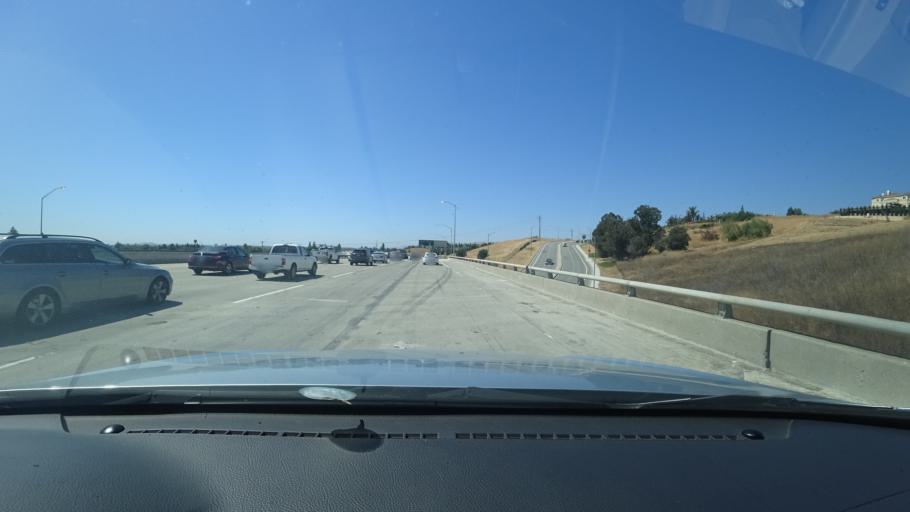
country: US
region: California
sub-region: Santa Clara County
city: Milpitas
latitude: 37.4907
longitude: -121.9183
